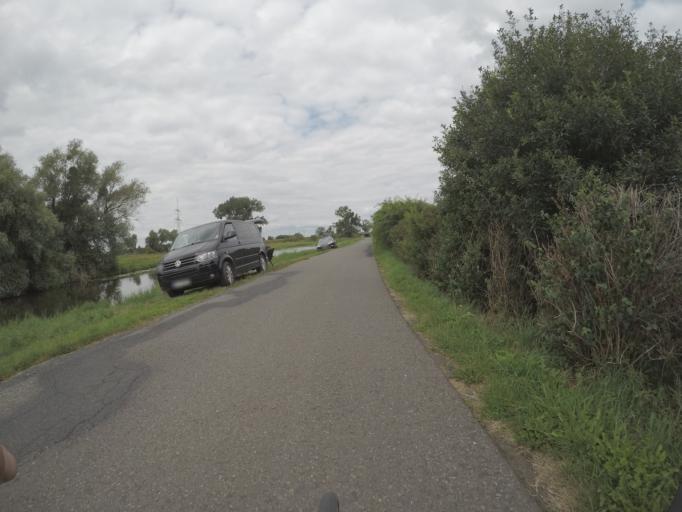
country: DE
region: Brandenburg
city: Wustermark
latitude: 52.5972
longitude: 12.9346
